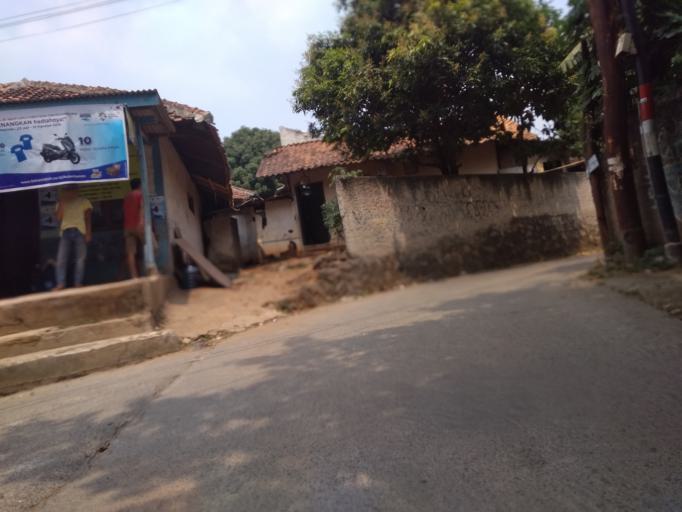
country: ID
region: West Java
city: Pamulang
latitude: -6.3216
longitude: 106.7912
